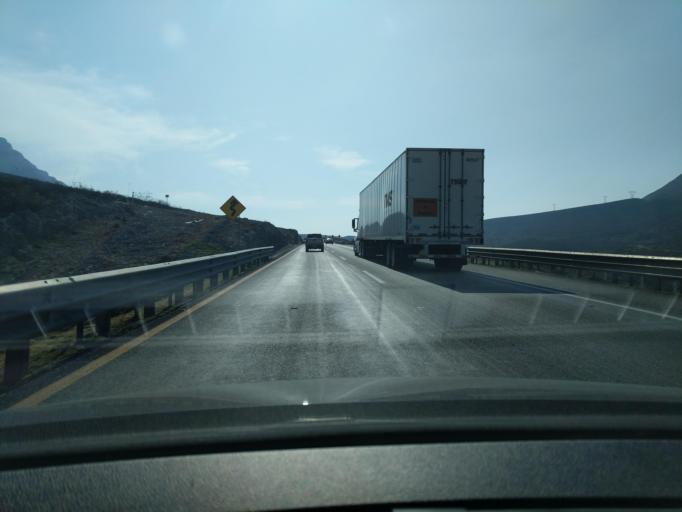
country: MX
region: Nuevo Leon
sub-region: Garcia
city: Las Torres de Guadalupe
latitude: 25.6536
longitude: -100.7248
